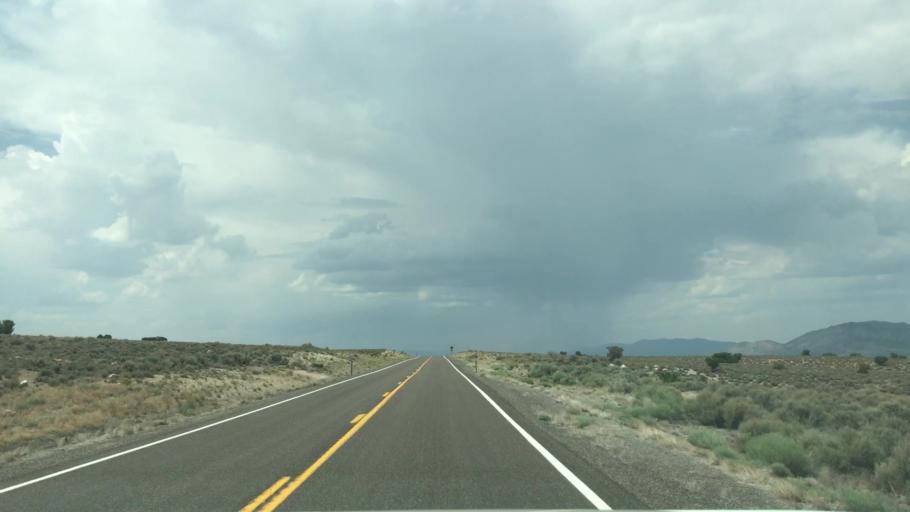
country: US
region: Nevada
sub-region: Eureka County
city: Eureka
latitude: 39.3962
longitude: -115.7173
